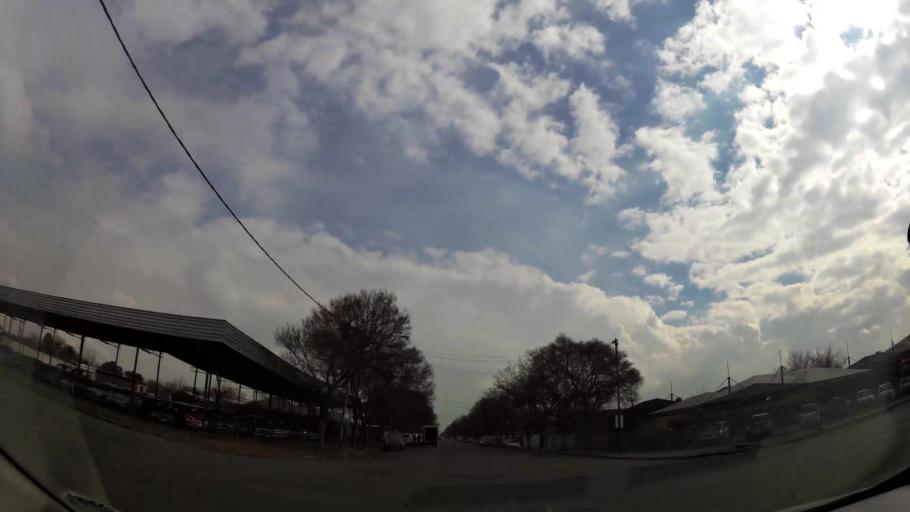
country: ZA
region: Gauteng
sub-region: Sedibeng District Municipality
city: Vereeniging
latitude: -26.6800
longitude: 27.9282
